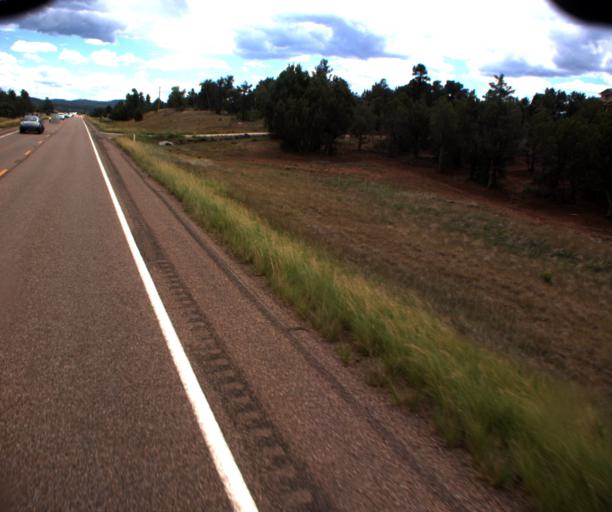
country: US
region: Arizona
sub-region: Navajo County
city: Linden
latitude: 34.3242
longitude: -110.2561
